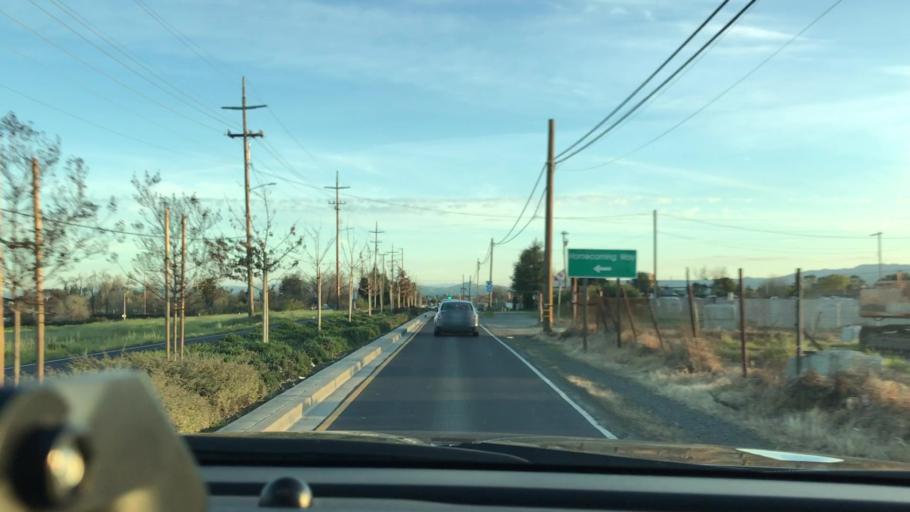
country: US
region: California
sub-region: Contra Costa County
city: Brentwood
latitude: 37.9572
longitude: -121.6962
